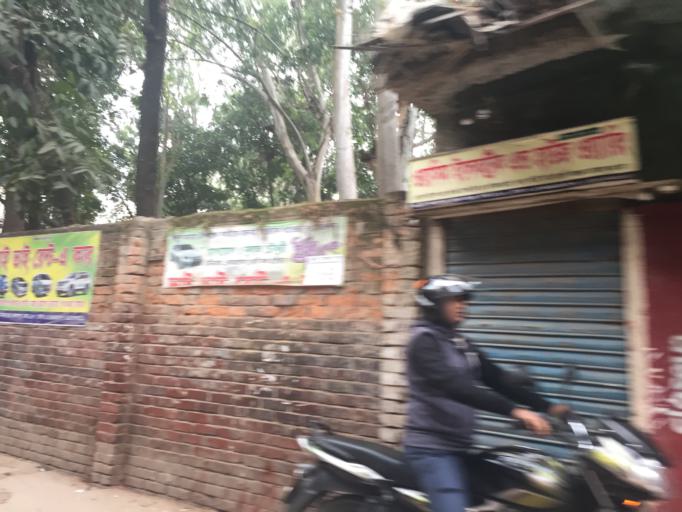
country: BD
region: Dhaka
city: Azimpur
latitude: 23.7808
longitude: 90.3605
